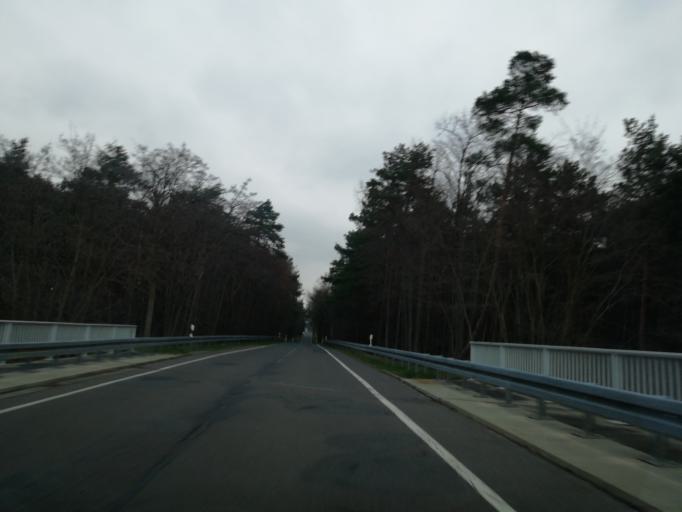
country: DE
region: Brandenburg
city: Vetschau
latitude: 51.7606
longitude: 14.1302
